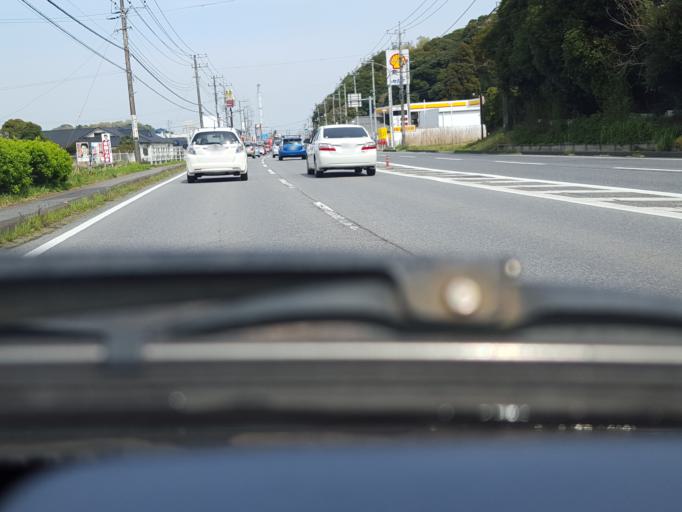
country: JP
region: Chiba
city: Ichihara
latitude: 35.4638
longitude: 140.0463
